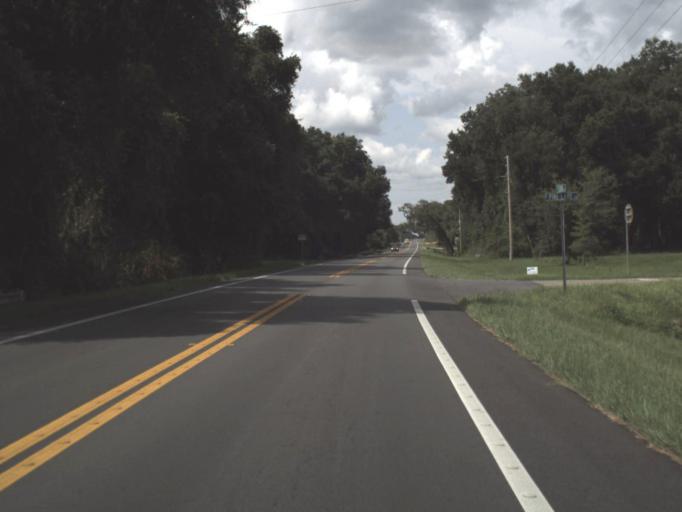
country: US
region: Florida
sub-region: Citrus County
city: Floral City
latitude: 28.7254
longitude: -82.3060
